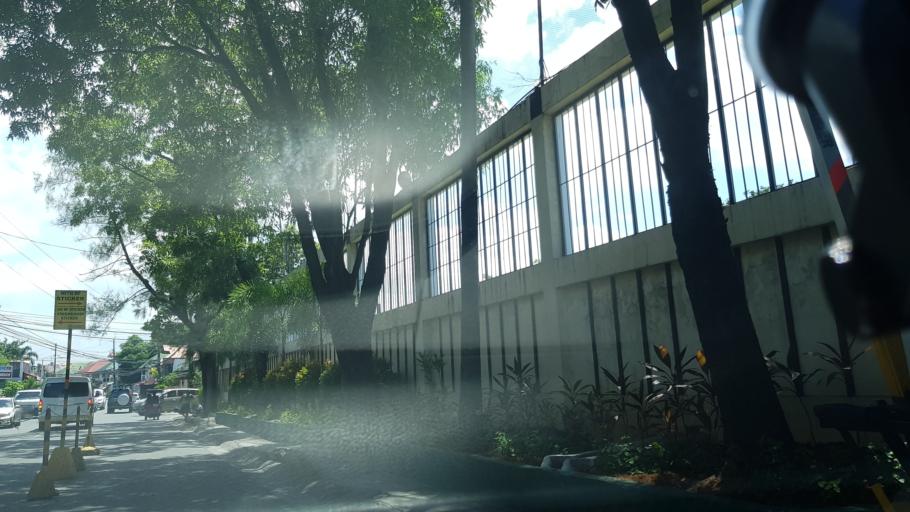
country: PH
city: Sambayanihan People's Village
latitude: 14.4547
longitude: 120.9957
